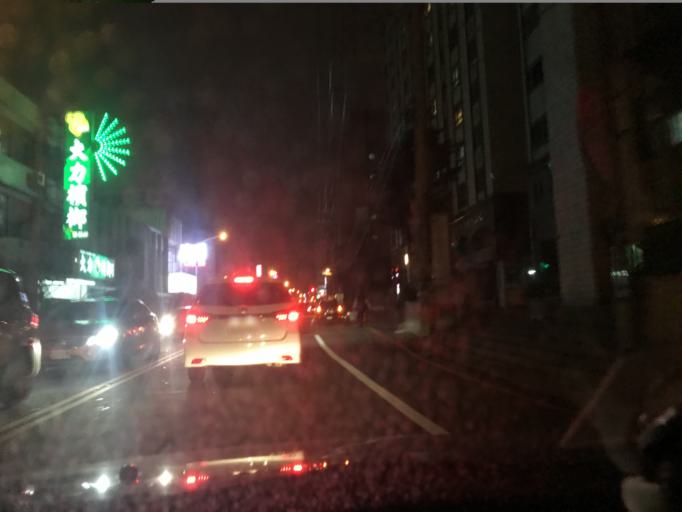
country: TW
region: Taiwan
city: Taoyuan City
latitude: 24.9623
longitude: 121.2306
